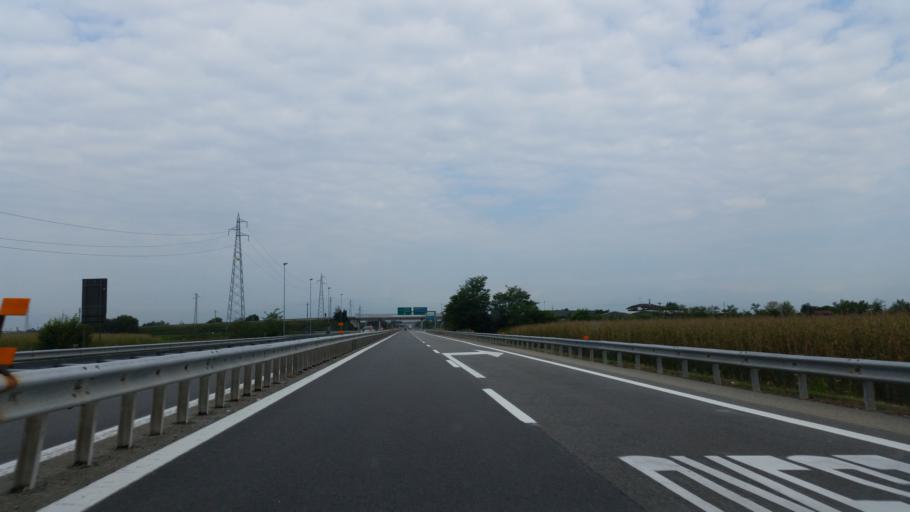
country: IT
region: Piedmont
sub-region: Provincia di Torino
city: Torrazza Piemonte
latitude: 45.2107
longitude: 7.9411
